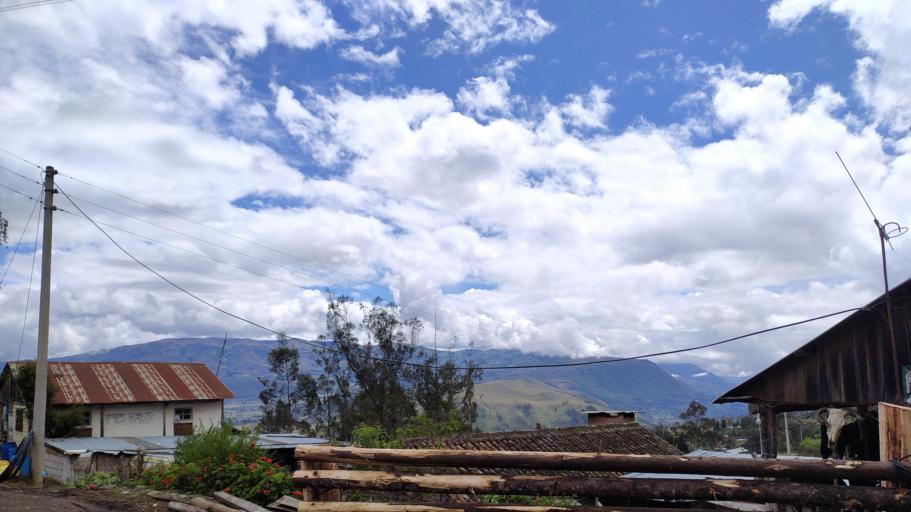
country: EC
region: Chimborazo
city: Riobamba
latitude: -1.6679
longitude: -78.5685
